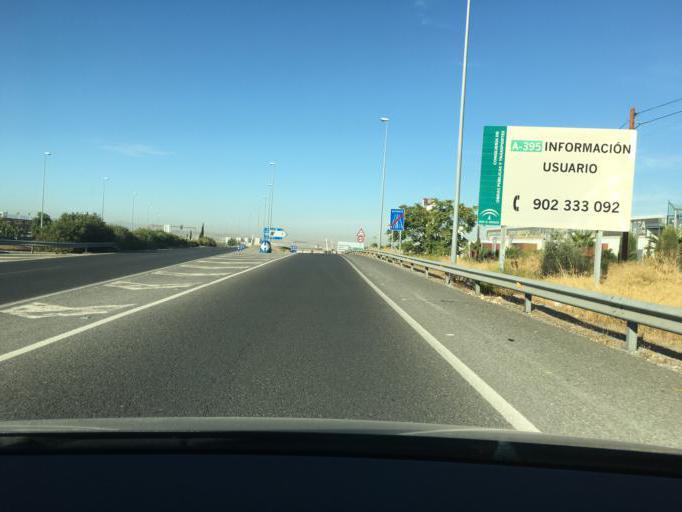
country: ES
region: Andalusia
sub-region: Provincia de Granada
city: Huetor Vega
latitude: 37.1565
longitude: -3.5822
